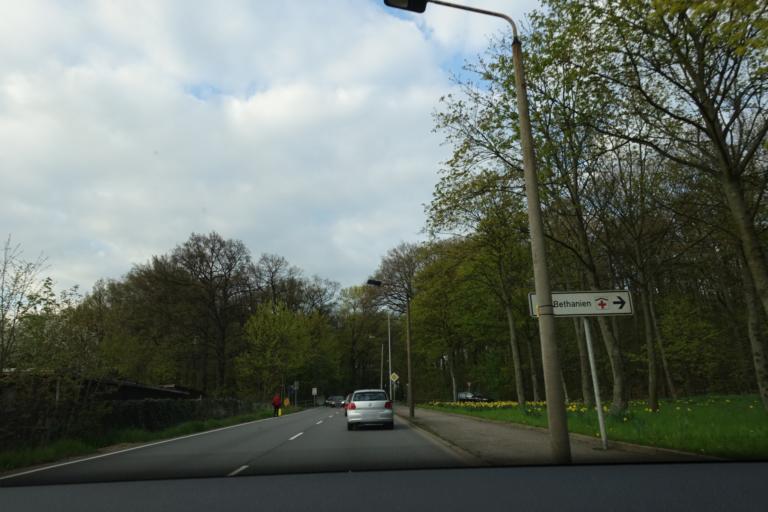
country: DE
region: Saxony
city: Hilbersdorf
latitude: 50.8533
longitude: 12.9575
